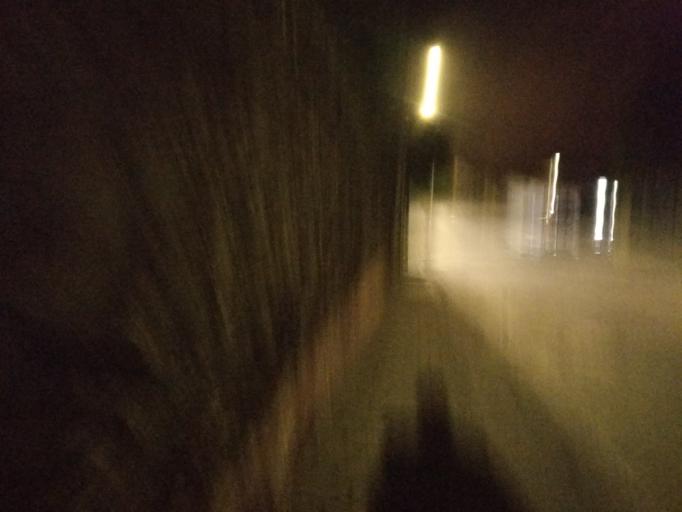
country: PT
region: Porto
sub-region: Vila Nova de Gaia
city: Vilar de Andorinho
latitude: 41.1089
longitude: -8.6030
